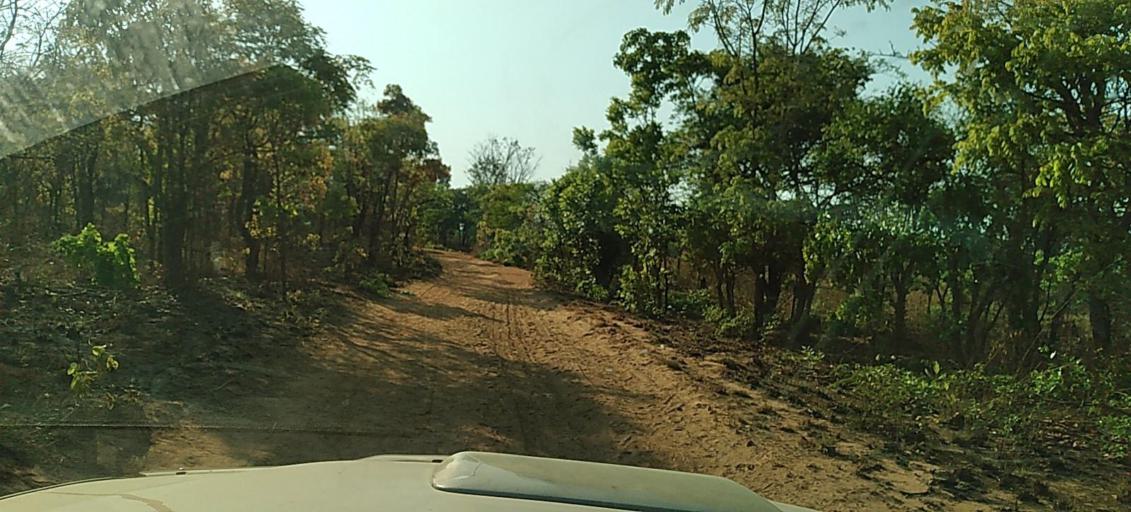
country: ZM
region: North-Western
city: Kasempa
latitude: -13.1851
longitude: 25.9567
